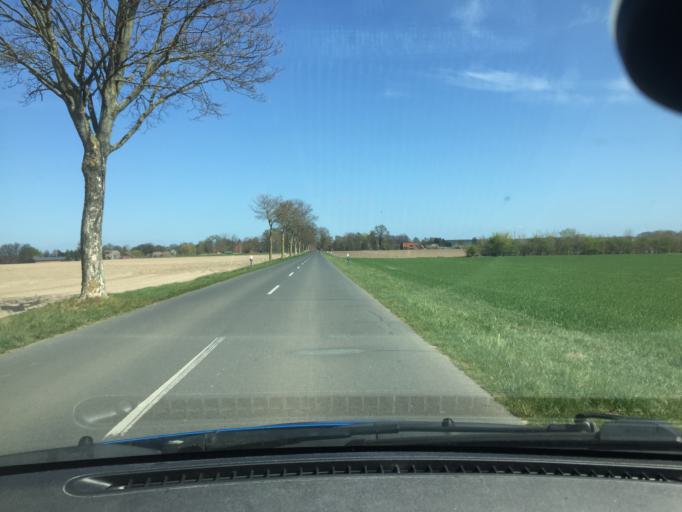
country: DE
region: Lower Saxony
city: Ratzlingen
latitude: 52.9494
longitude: 10.6640
